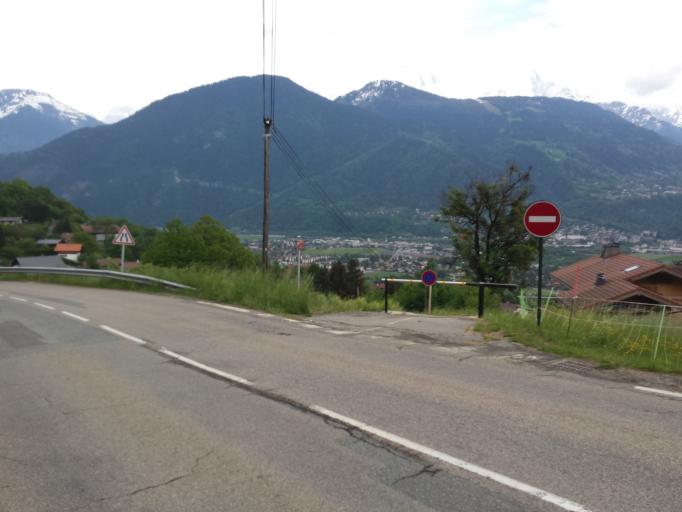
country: FR
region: Rhone-Alpes
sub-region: Departement de la Haute-Savoie
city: Passy
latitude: 45.9252
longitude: 6.6836
